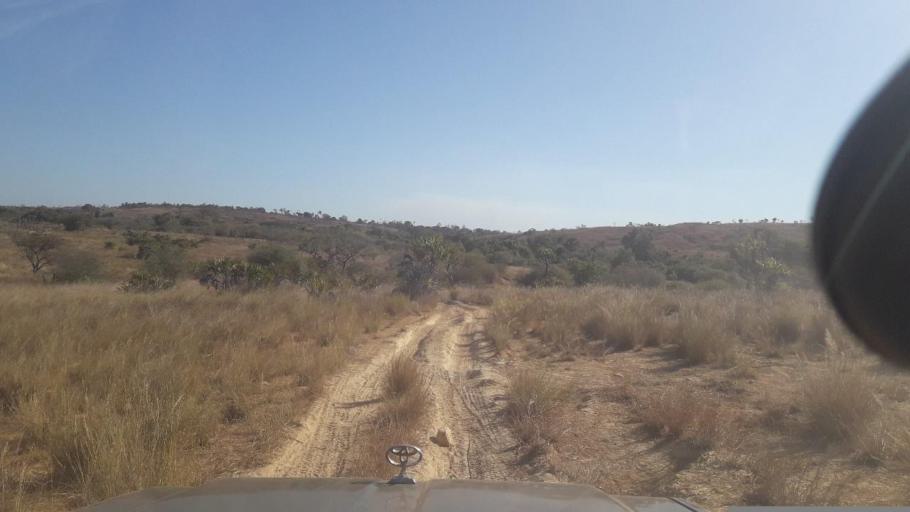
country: MG
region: Boeny
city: Sitampiky
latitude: -16.3756
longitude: 45.5909
